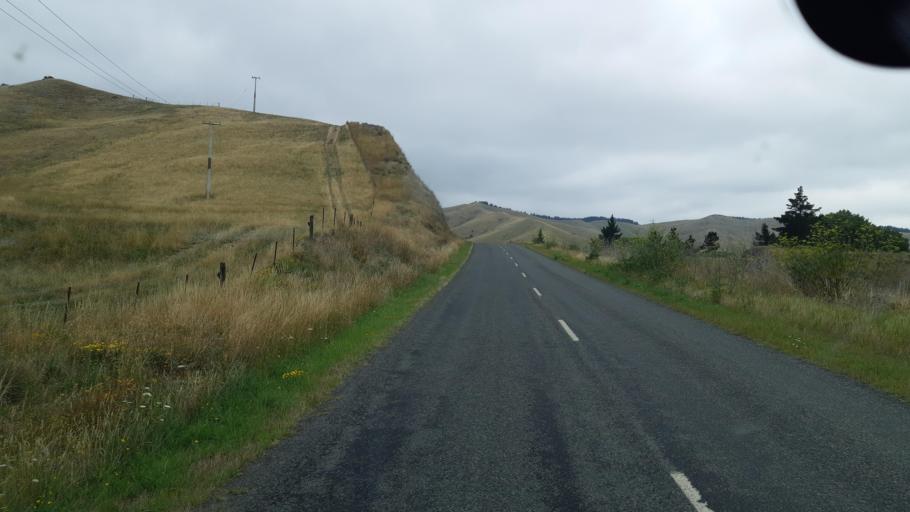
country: NZ
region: Marlborough
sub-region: Marlborough District
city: Blenheim
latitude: -41.5697
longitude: 173.9313
